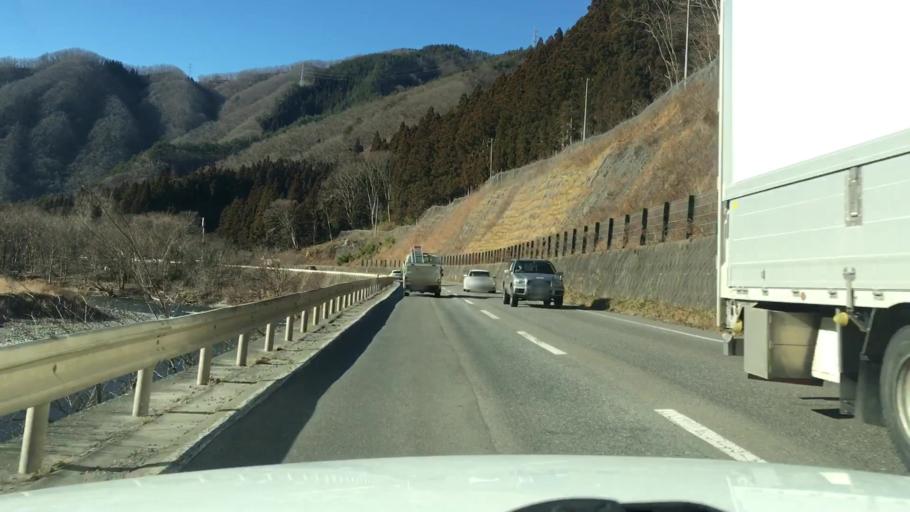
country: JP
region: Iwate
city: Miyako
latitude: 39.6270
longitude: 141.8230
